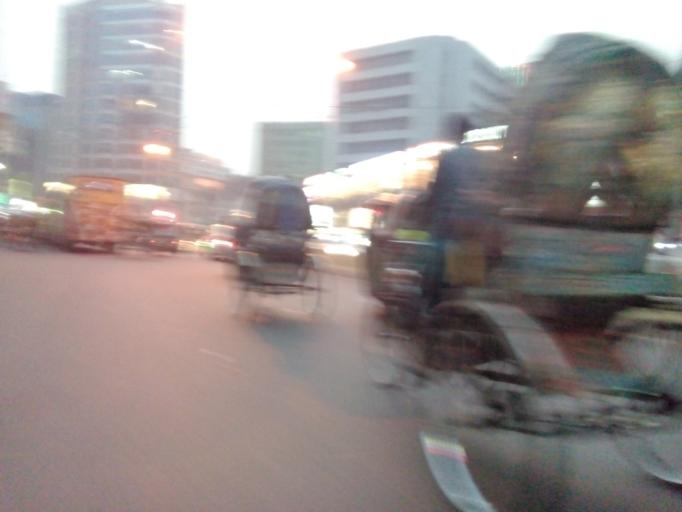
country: BD
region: Dhaka
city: Paltan
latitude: 23.7382
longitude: 90.4094
